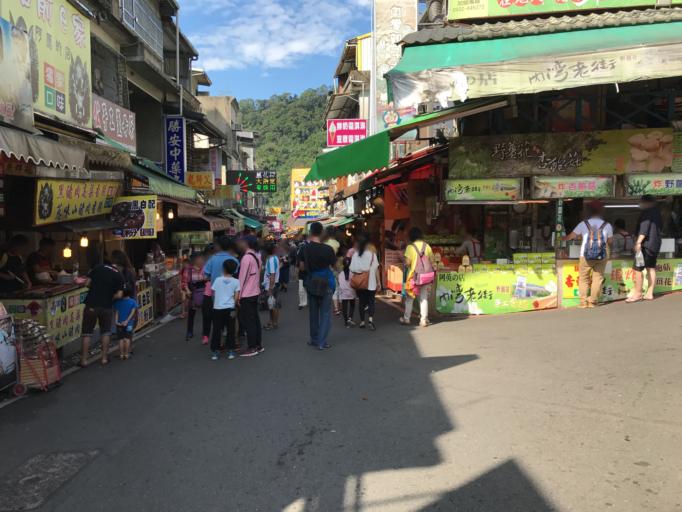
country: TW
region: Taiwan
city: Daxi
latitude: 24.7053
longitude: 121.1823
